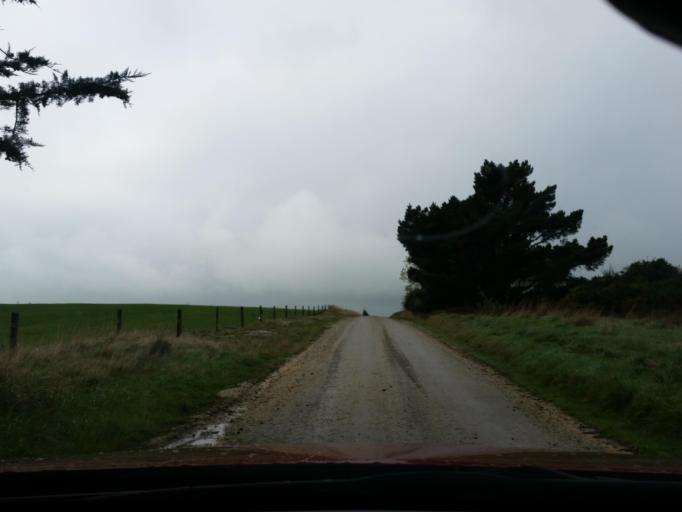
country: NZ
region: Southland
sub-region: Invercargill City
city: Invercargill
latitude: -46.2849
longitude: 168.5565
